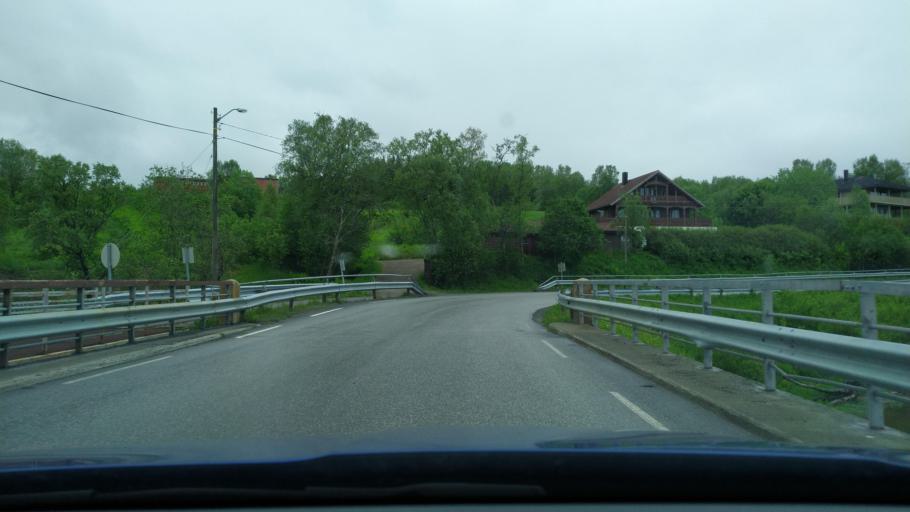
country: NO
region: Troms
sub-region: Dyroy
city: Brostadbotn
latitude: 69.0865
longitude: 17.6963
